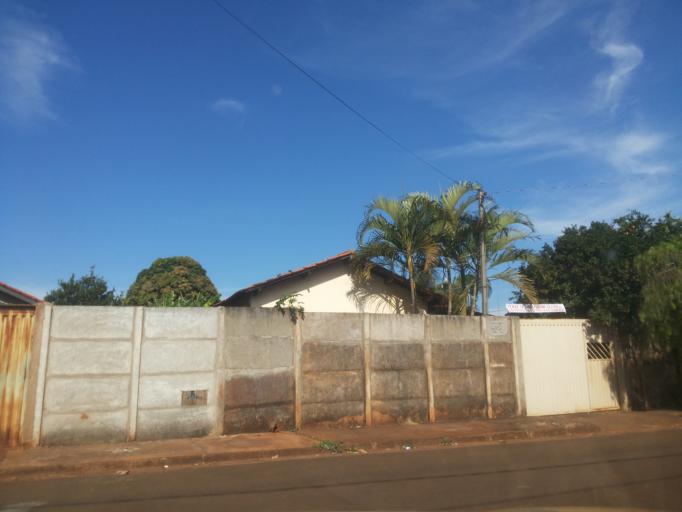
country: BR
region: Minas Gerais
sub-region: Centralina
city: Centralina
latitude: -18.7173
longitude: -49.2038
